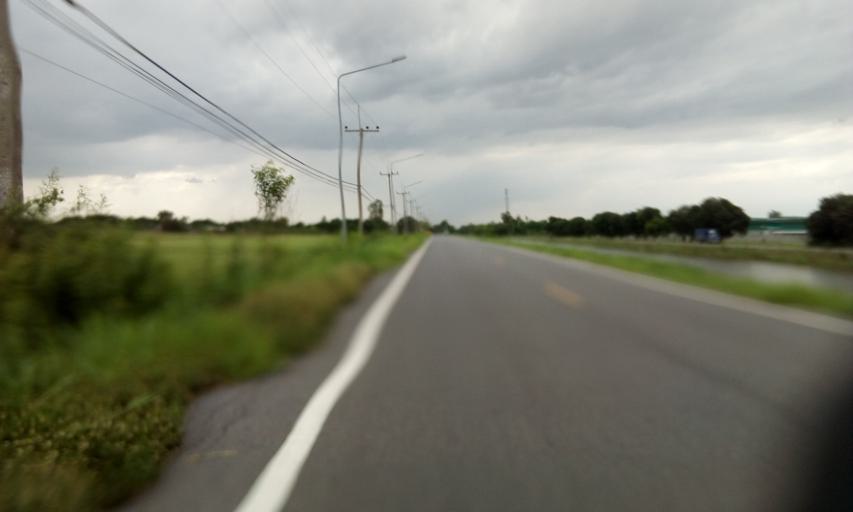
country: TH
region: Pathum Thani
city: Nong Suea
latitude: 14.0720
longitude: 100.8463
